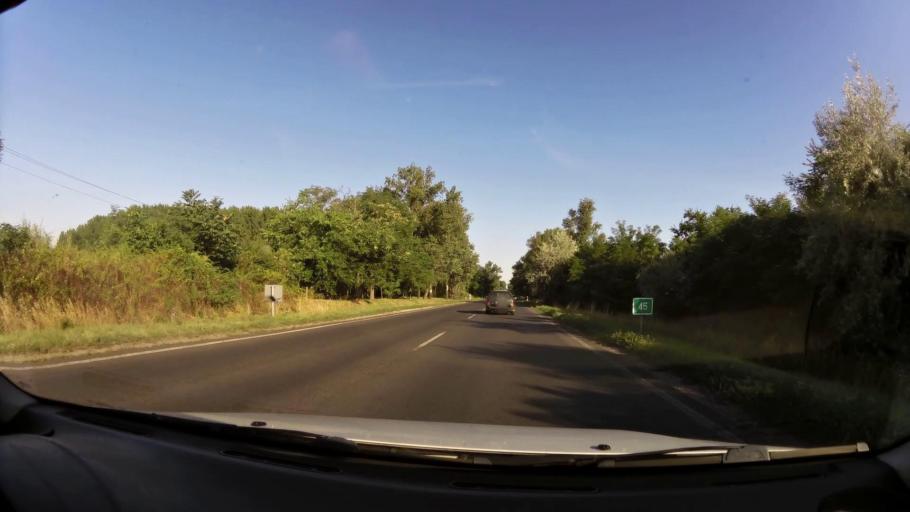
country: HU
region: Pest
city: Pilis
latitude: 47.2930
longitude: 19.5333
